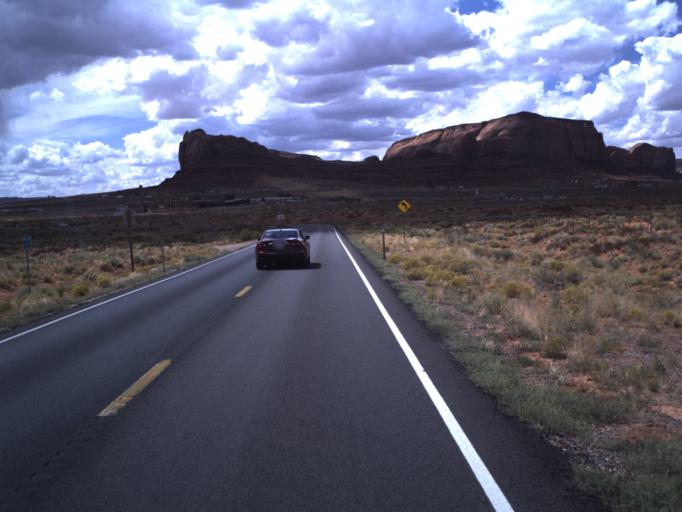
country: US
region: Arizona
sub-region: Navajo County
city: Kayenta
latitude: 37.0108
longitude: -110.1683
